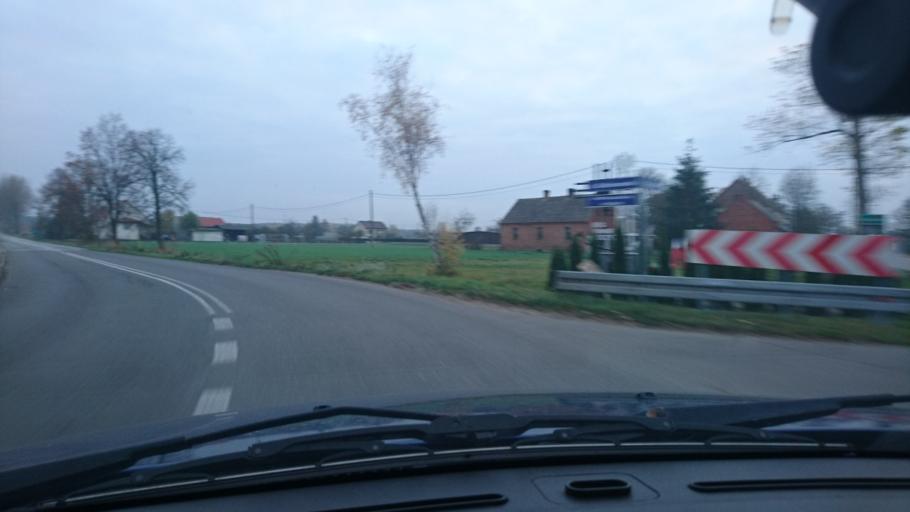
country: PL
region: Greater Poland Voivodeship
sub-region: Powiat ostrowski
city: Odolanow
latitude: 51.5417
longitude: 17.6515
